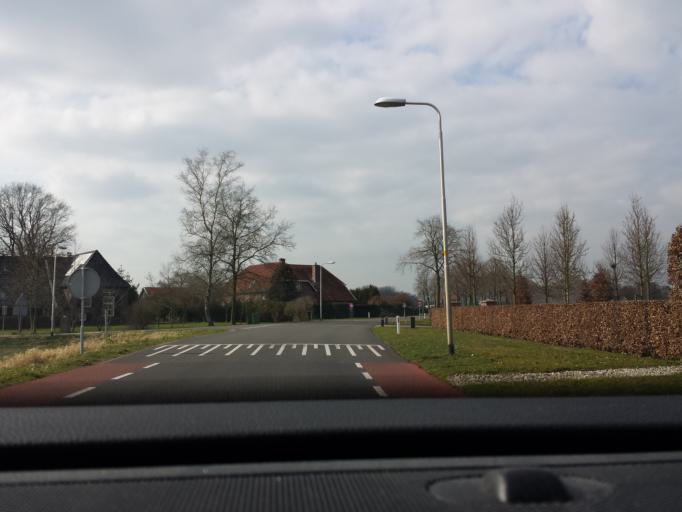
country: NL
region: Gelderland
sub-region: Oost Gelre
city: Lichtenvoorde
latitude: 52.0124
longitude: 6.5066
